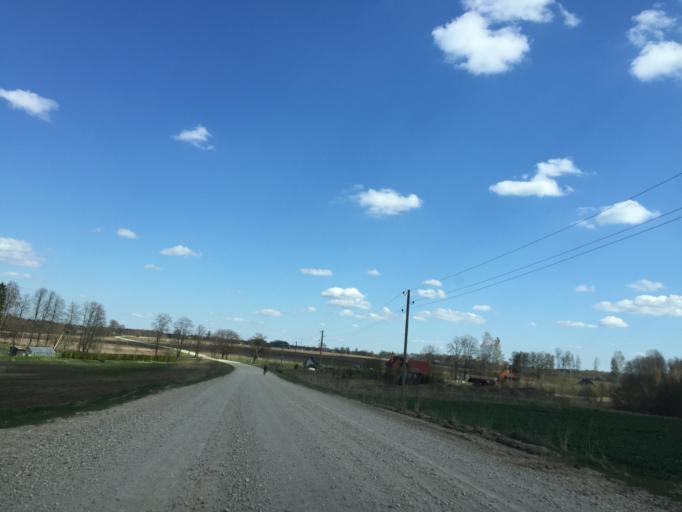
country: LV
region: Seja
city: Loja
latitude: 57.2637
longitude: 24.5616
